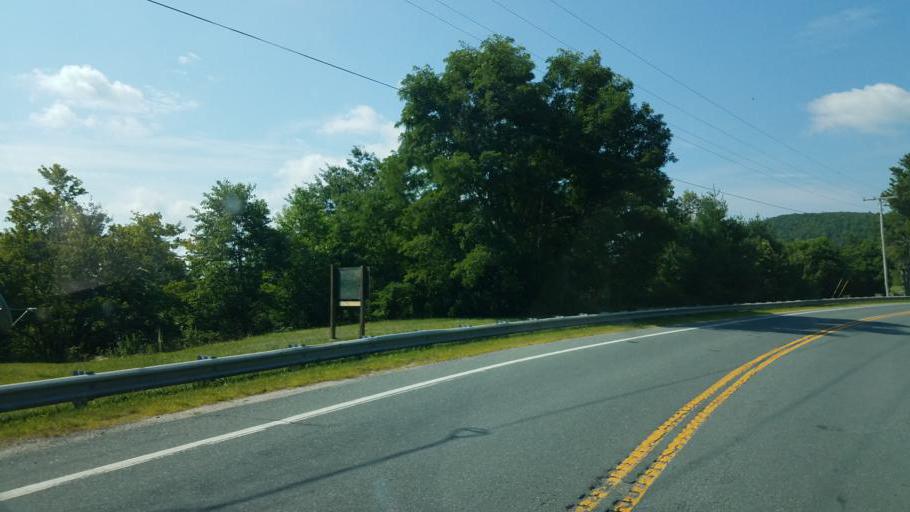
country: US
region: North Carolina
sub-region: Avery County
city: Newland
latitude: 35.9757
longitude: -81.8928
